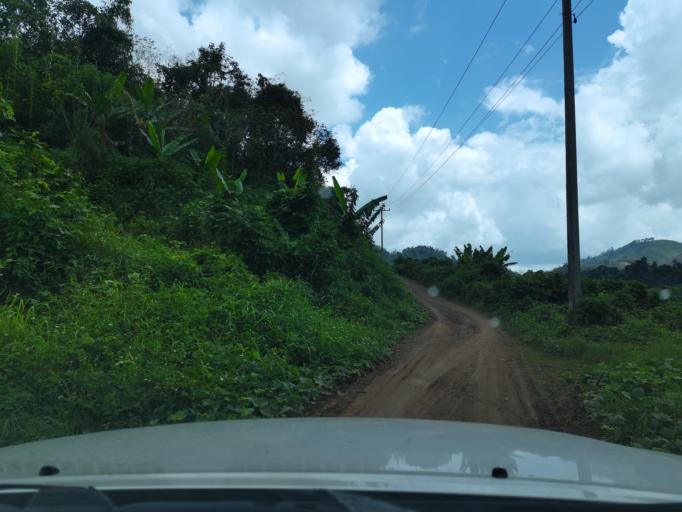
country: LA
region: Loungnamtha
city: Muang Long
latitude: 20.7527
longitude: 101.0182
